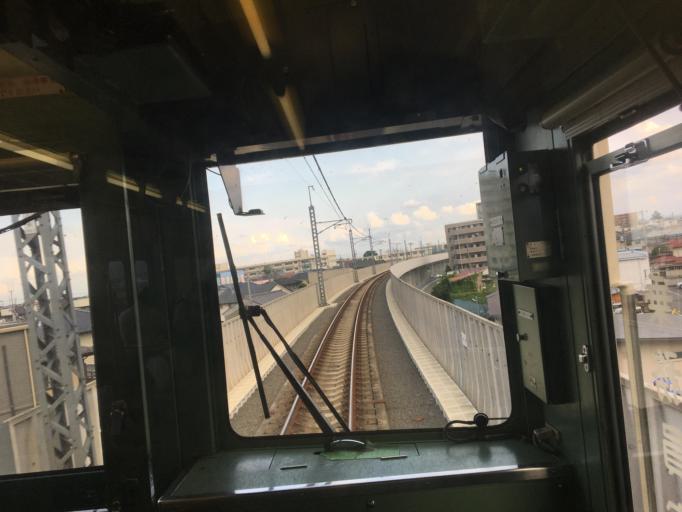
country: JP
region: Gunma
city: Isesaki
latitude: 36.3247
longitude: 139.1993
